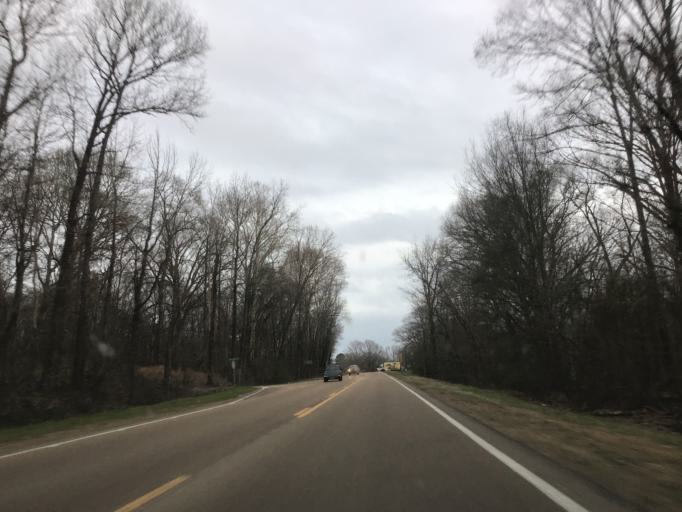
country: US
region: Mississippi
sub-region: Warren County
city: Beechwood
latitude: 32.2996
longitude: -90.7983
